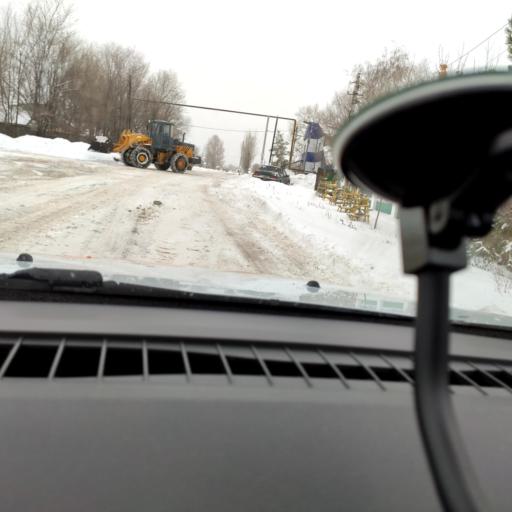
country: RU
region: Samara
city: Dubovyy Umet
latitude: 53.0390
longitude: 50.2427
